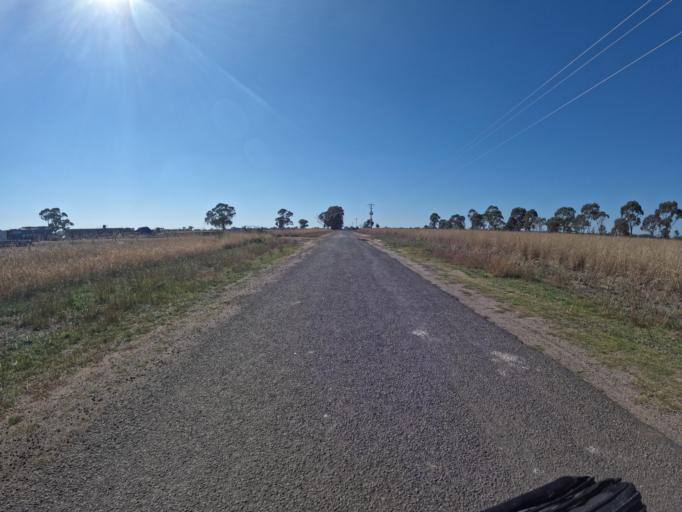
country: AU
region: Victoria
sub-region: Greater Bendigo
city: Epsom
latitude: -36.7893
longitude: 144.5142
